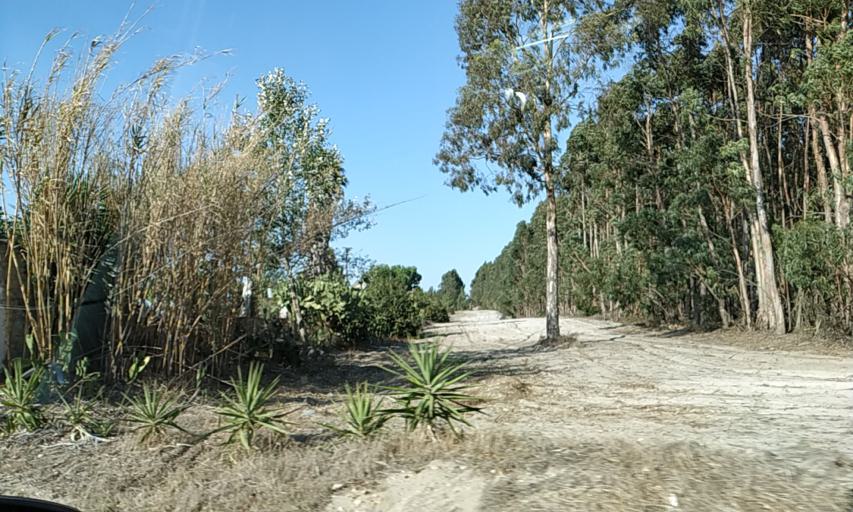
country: PT
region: Santarem
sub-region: Almeirim
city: Fazendas de Almeirim
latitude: 39.1454
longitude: -8.6151
